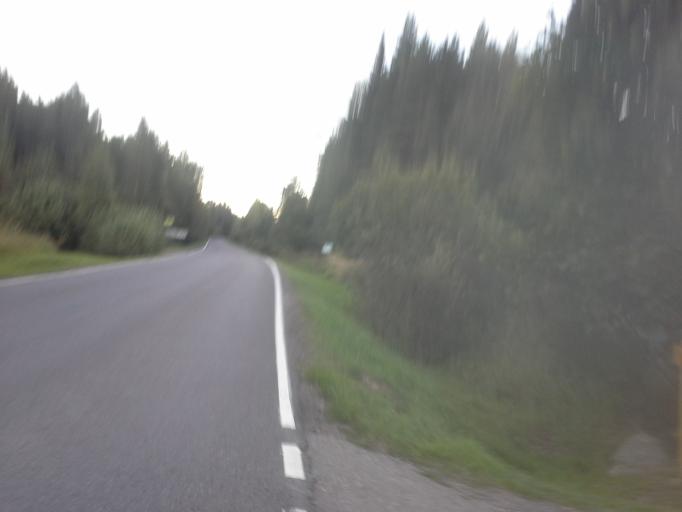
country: RU
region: Moskovskaya
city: Selyatino
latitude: 55.5087
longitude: 36.9357
